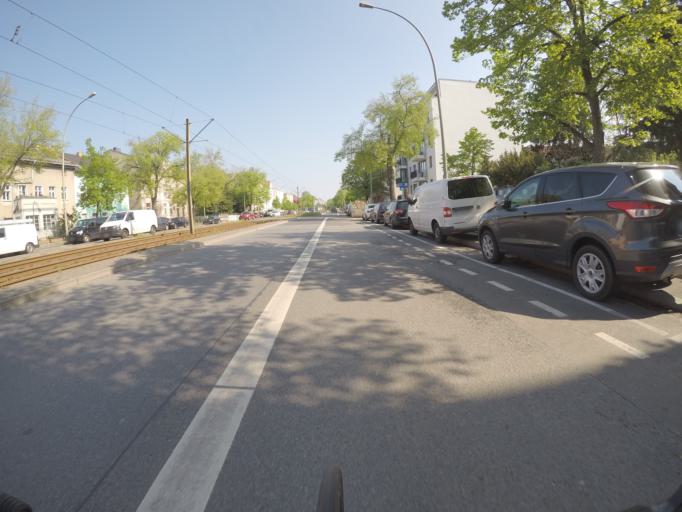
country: DE
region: Berlin
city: Buchholz
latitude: 52.5945
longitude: 13.4324
